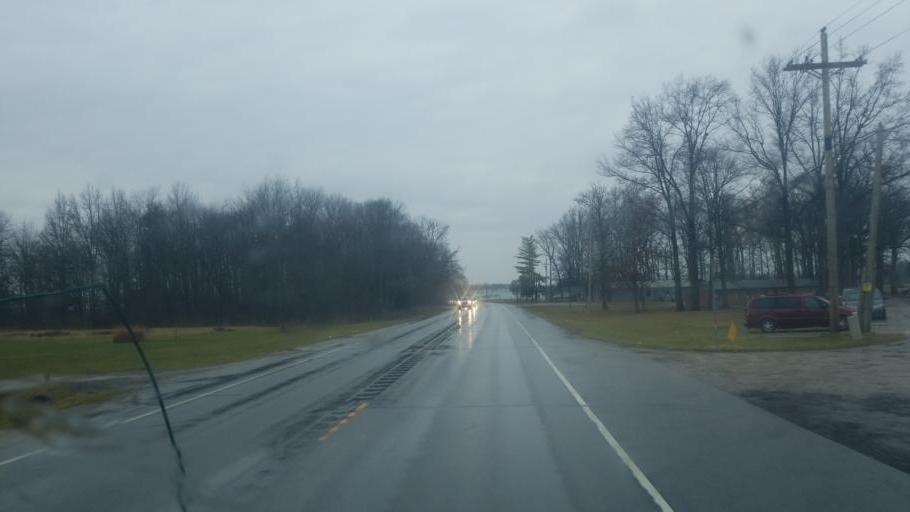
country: US
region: Indiana
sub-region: Bartholomew County
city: Columbus
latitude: 39.1925
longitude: -85.8543
